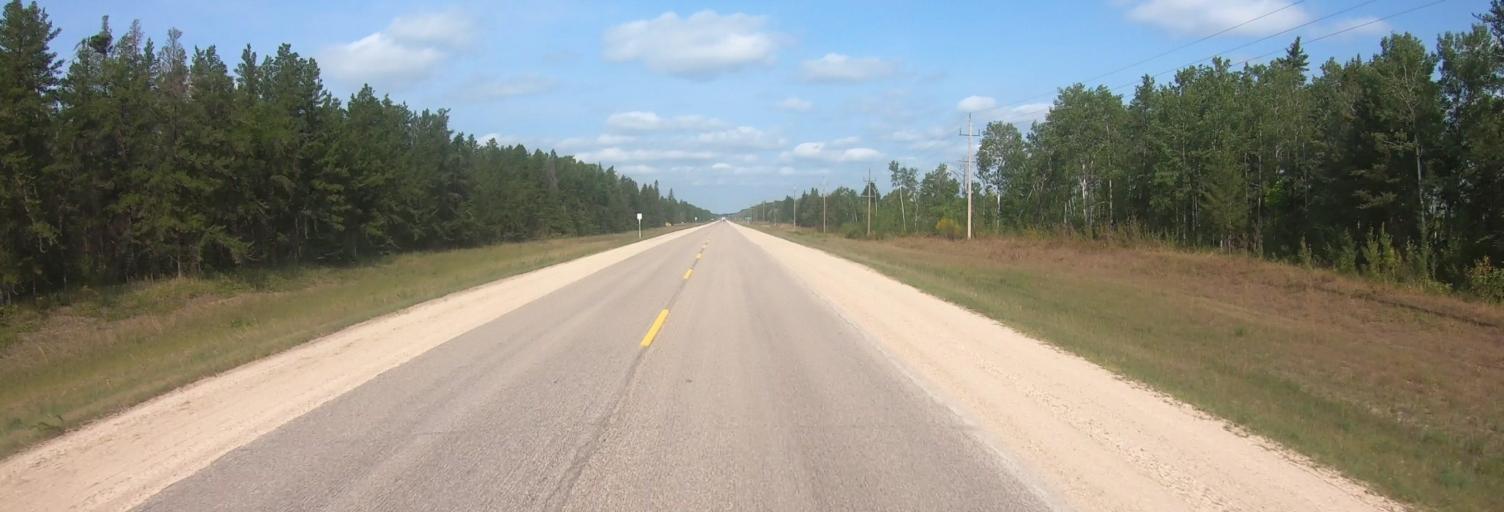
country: CA
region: Manitoba
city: La Broquerie
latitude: 49.1905
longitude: -96.2556
